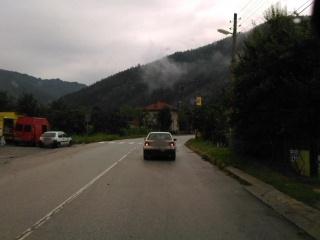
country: BG
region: Lovech
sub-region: Obshtina Troyan
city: Troyan
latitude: 42.8633
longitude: 24.6945
